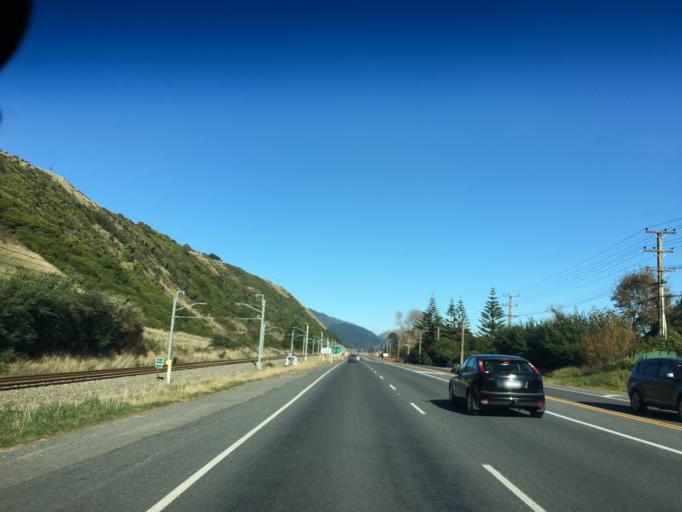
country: NZ
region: Wellington
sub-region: Kapiti Coast District
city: Paraparaumu
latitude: -40.9303
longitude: 174.9974
